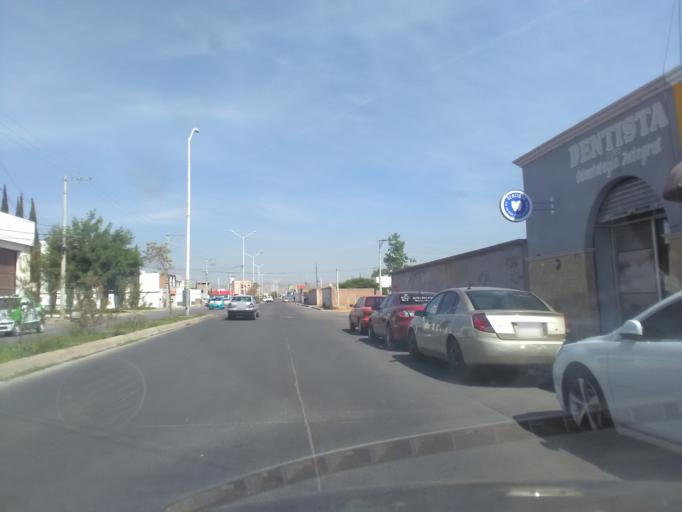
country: MX
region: Durango
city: Victoria de Durango
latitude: 24.0543
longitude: -104.6279
